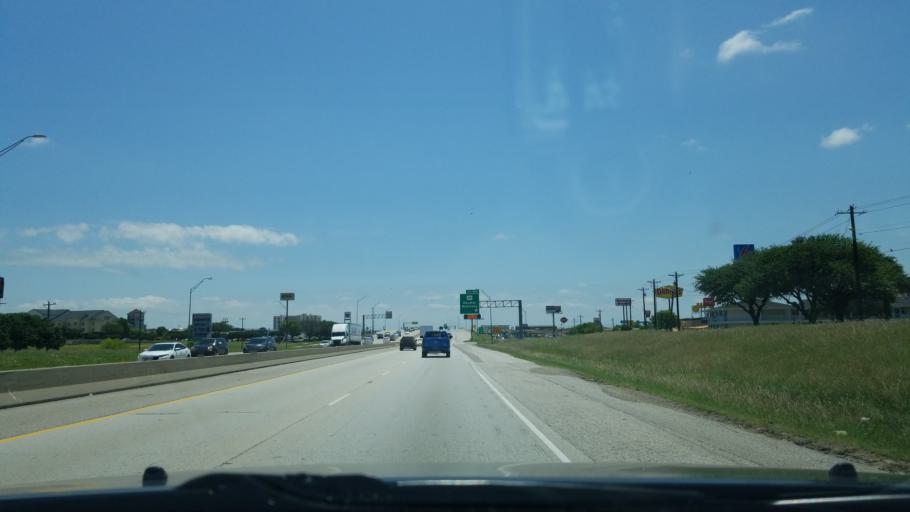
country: US
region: Texas
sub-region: Denton County
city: Denton
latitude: 33.2342
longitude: -97.1755
